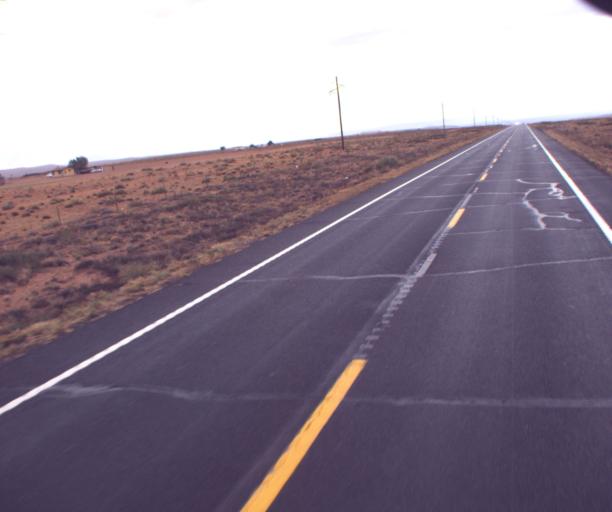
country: US
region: Arizona
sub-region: Coconino County
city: Tuba City
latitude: 36.1459
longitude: -111.1468
